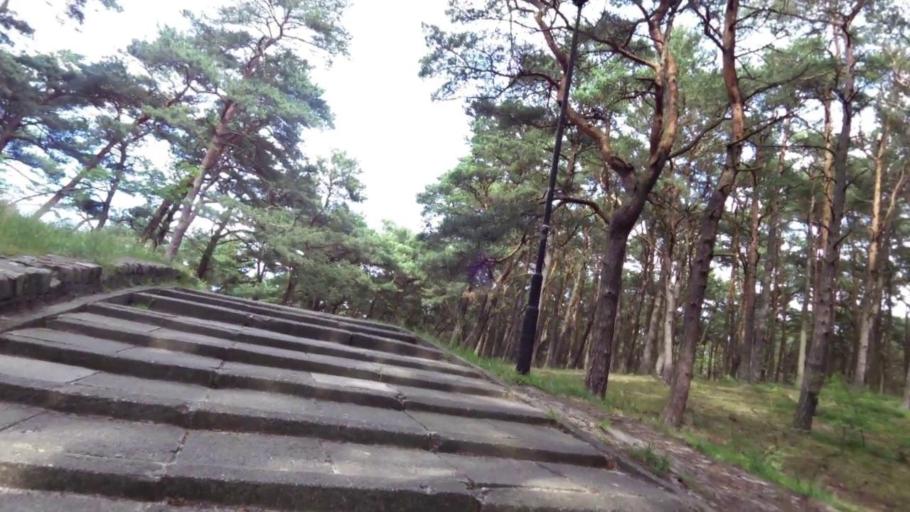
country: PL
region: West Pomeranian Voivodeship
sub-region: Powiat gryficki
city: Mrzezyno
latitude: 54.1462
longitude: 15.2941
